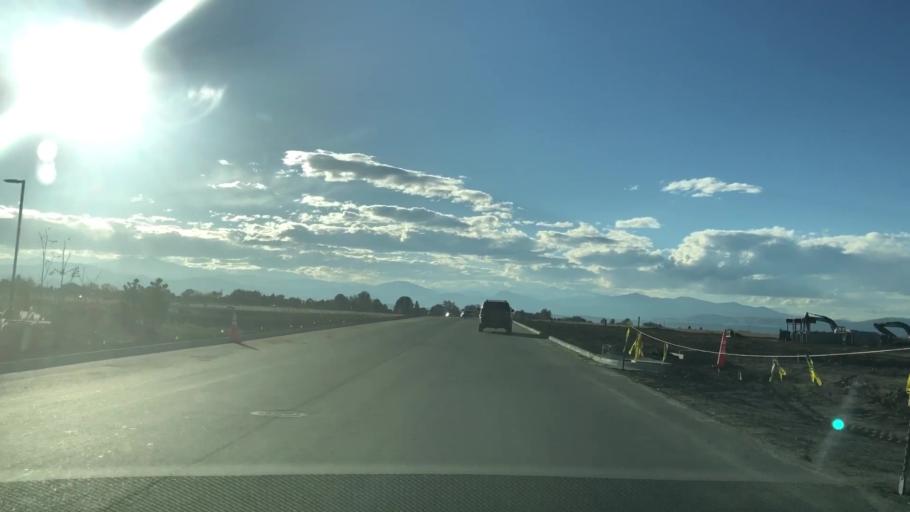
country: US
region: Colorado
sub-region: Larimer County
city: Loveland
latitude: 40.4304
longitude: -105.0109
